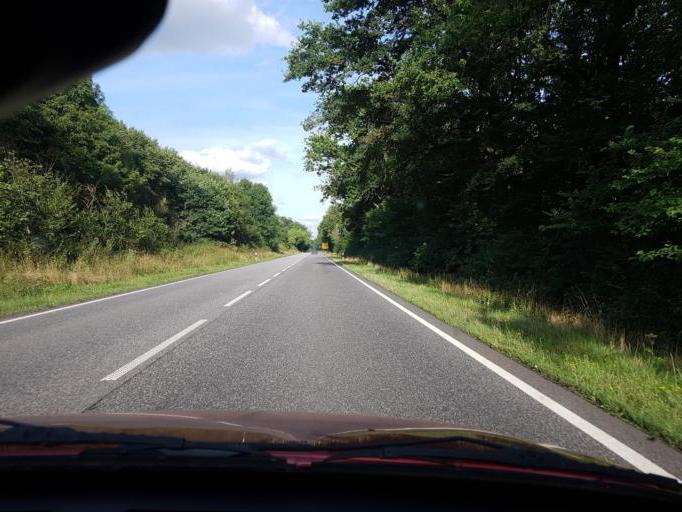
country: DE
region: Hesse
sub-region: Regierungsbezirk Giessen
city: Grossen Buseck
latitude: 50.5877
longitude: 8.7573
